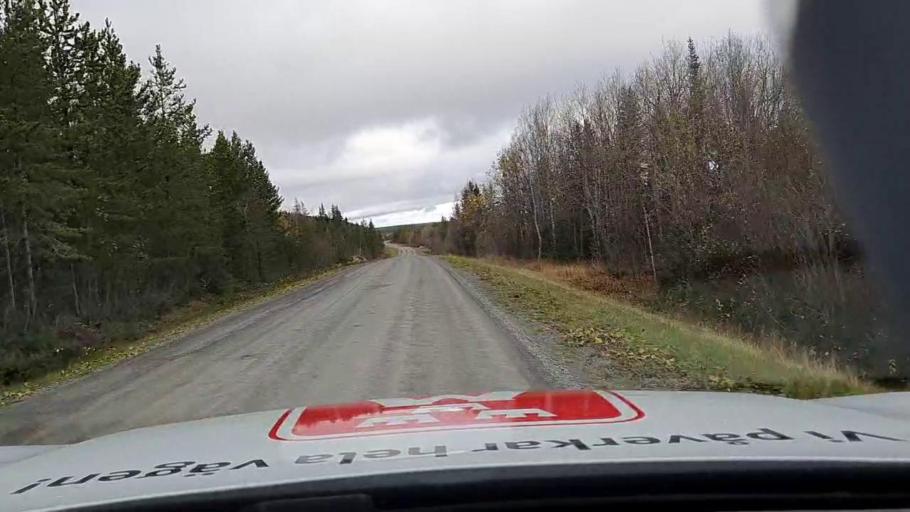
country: SE
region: Jaemtland
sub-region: Krokoms Kommun
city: Valla
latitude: 63.0571
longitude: 13.9630
